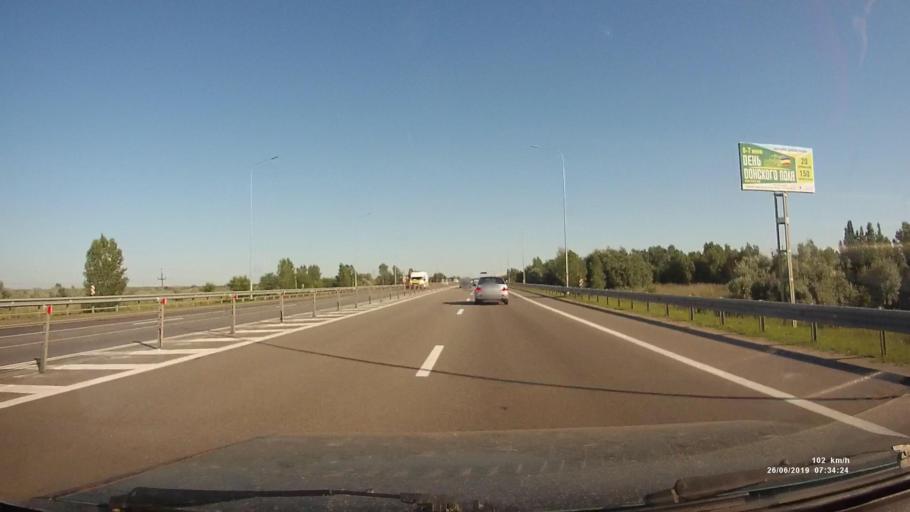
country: RU
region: Rostov
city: Bataysk
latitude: 47.1474
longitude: 39.6698
